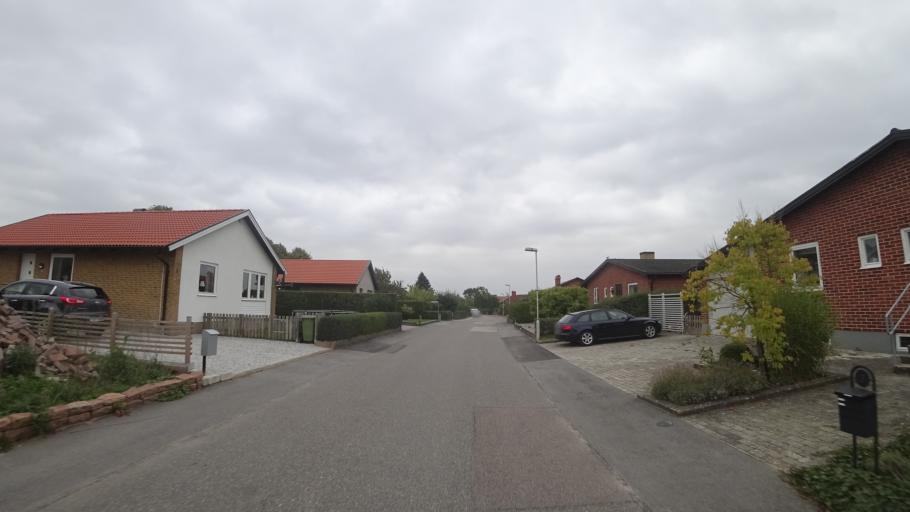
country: SE
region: Skane
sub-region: Kavlinge Kommun
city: Kaevlinge
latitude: 55.7900
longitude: 13.0869
